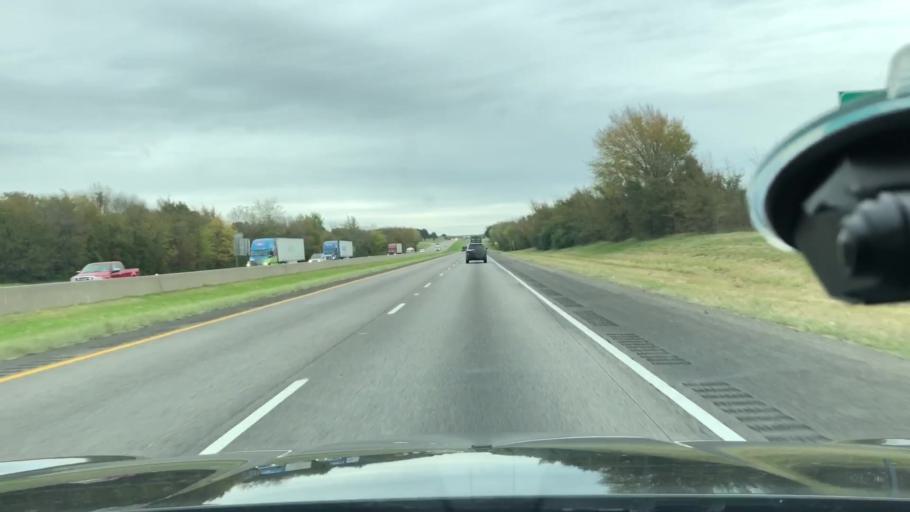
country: US
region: Texas
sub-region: Hopkins County
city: Sulphur Springs
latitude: 33.1582
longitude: -95.4168
